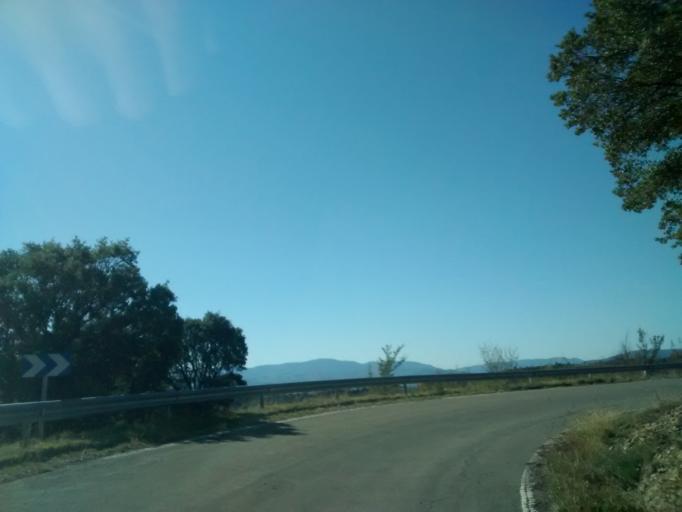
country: ES
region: Aragon
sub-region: Provincia de Huesca
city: Jaca
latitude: 42.4793
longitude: -0.5728
